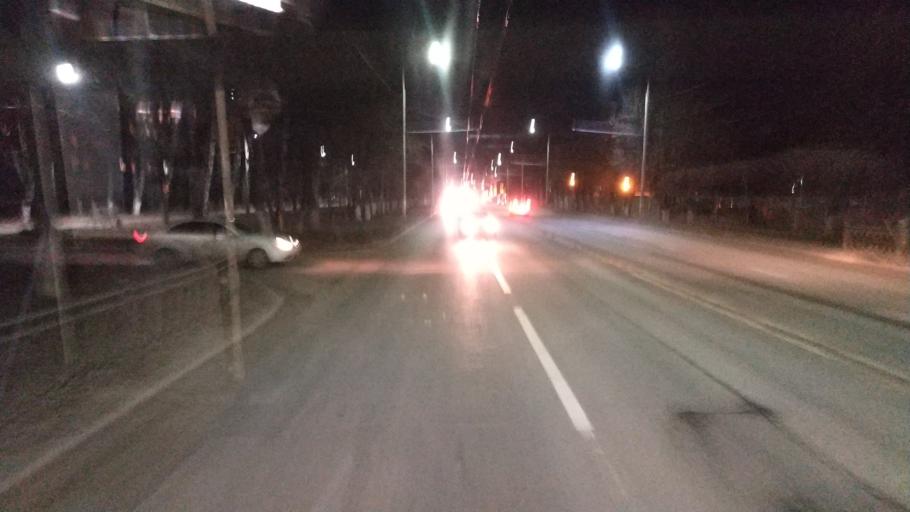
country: RU
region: Moskovskaya
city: Dubrovitsy
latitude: 55.4214
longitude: 37.5086
